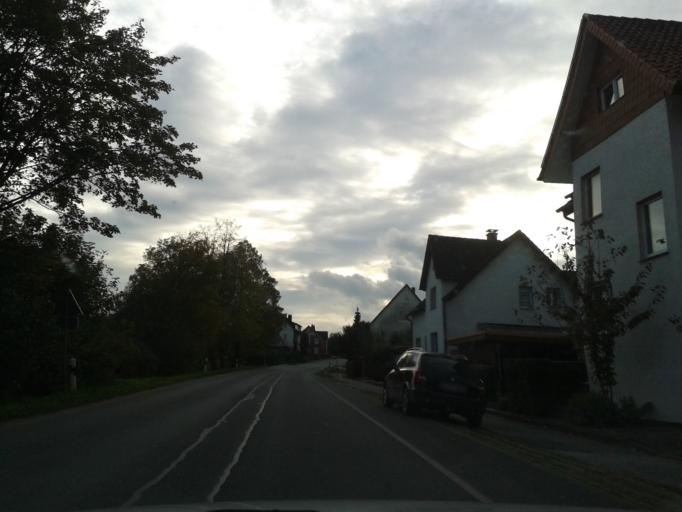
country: DE
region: North Rhine-Westphalia
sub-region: Regierungsbezirk Detmold
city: Bad Meinberg
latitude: 51.8920
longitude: 8.9722
